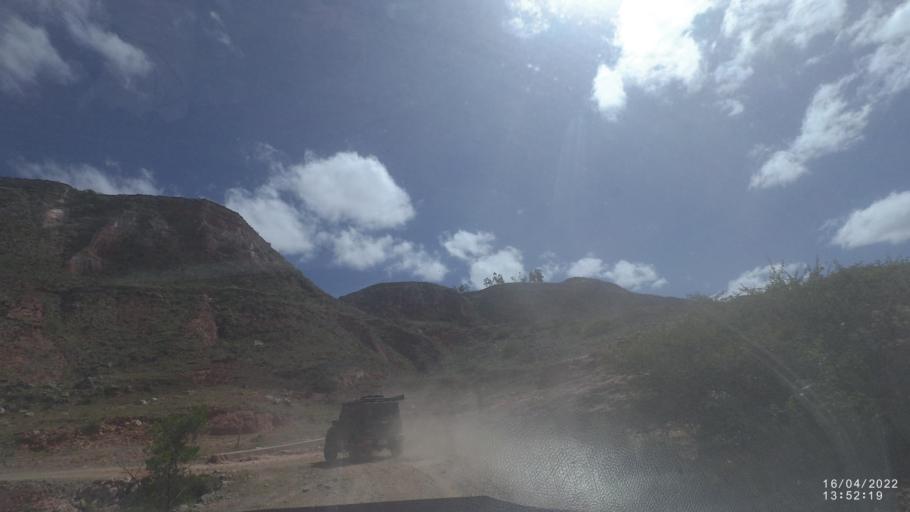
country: BO
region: Cochabamba
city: Mizque
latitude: -18.0218
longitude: -65.5743
